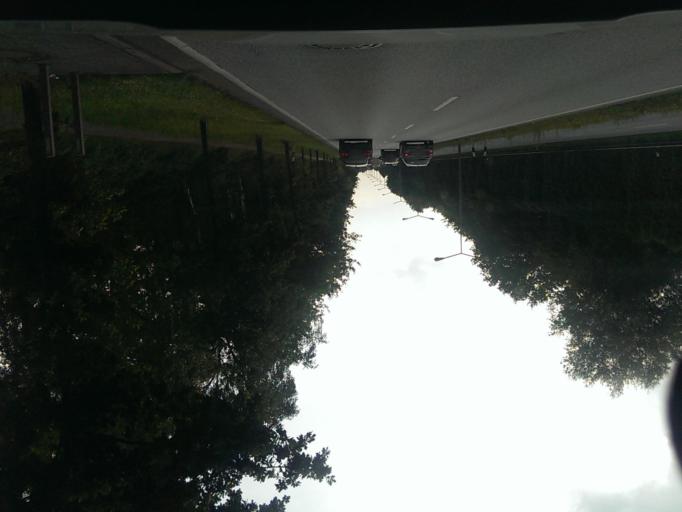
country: DE
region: Schleswig-Holstein
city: Bonningstedt
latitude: 53.6481
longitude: 9.9559
